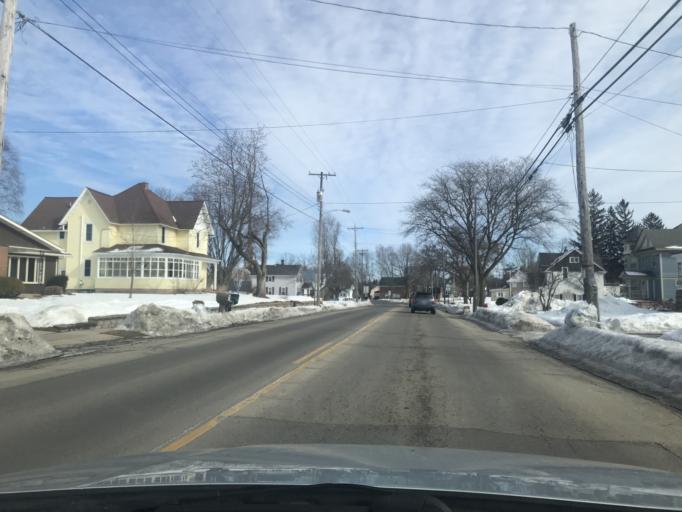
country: US
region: Wisconsin
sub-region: Oconto County
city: Gillett
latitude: 44.8889
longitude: -88.3102
